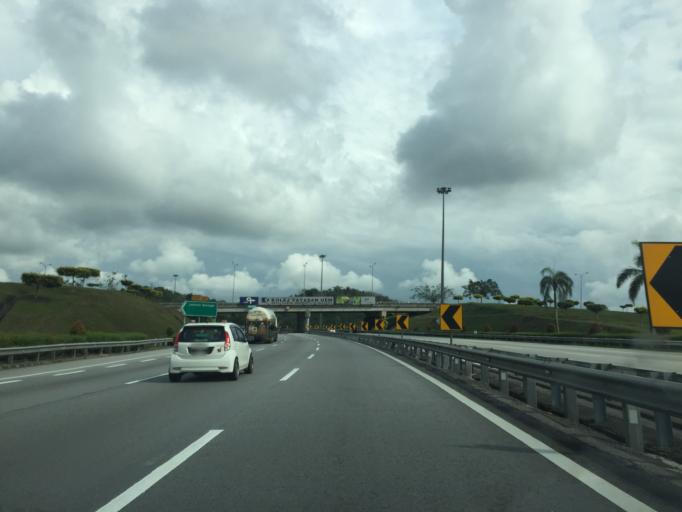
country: MY
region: Selangor
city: Batang Berjuntai
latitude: 3.5761
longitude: 101.5248
